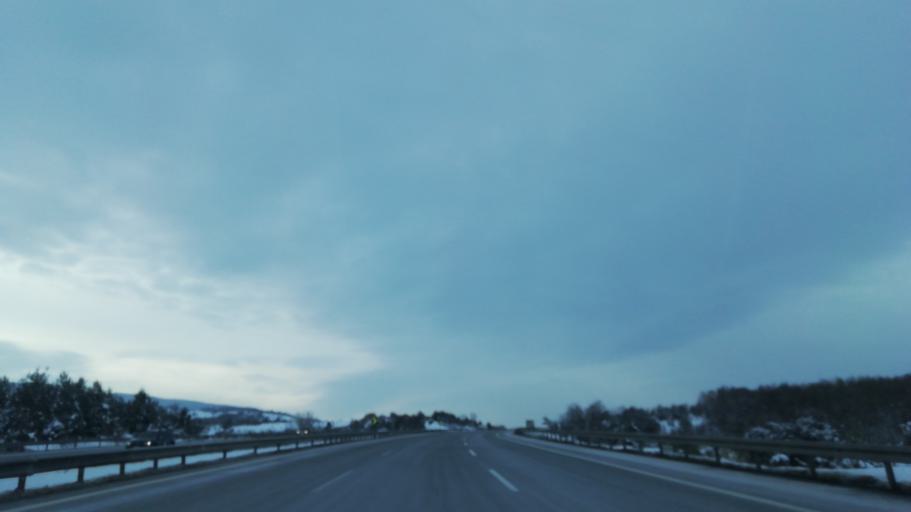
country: TR
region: Bolu
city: Yenicaga
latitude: 40.7538
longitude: 31.9603
